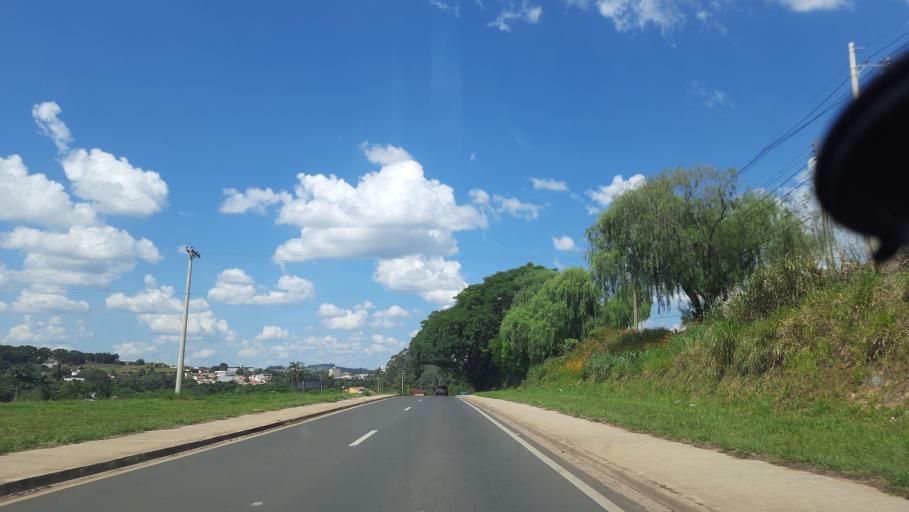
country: BR
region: Sao Paulo
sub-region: Sao Jose Do Rio Pardo
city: Sao Jose do Rio Pardo
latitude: -21.6019
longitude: -46.9085
